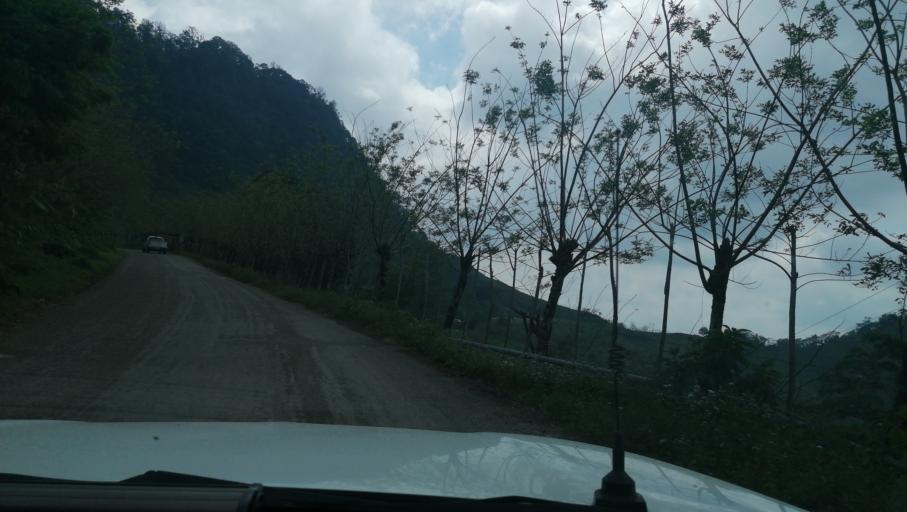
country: MX
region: Chiapas
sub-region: Francisco Leon
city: San Miguel la Sardina
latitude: 17.2474
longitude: -93.2860
